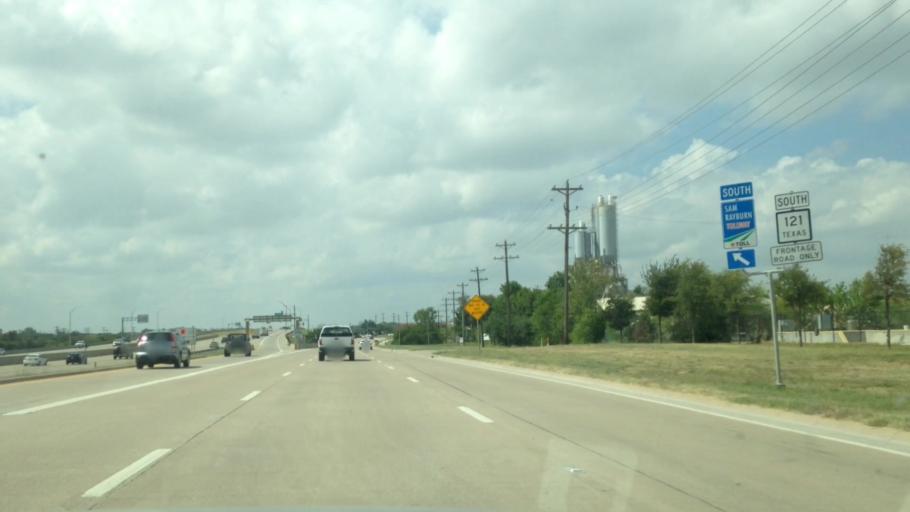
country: US
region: Texas
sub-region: Collin County
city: Allen
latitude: 33.1217
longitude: -96.7446
